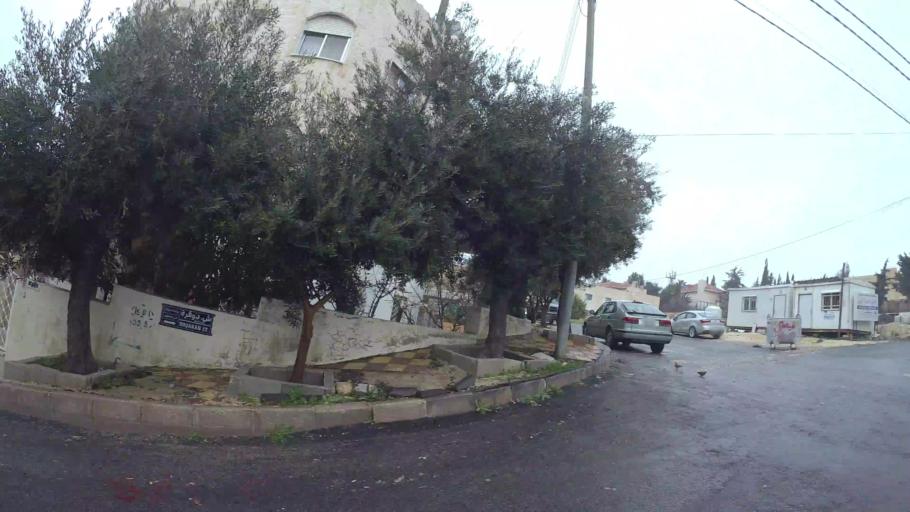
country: JO
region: Amman
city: Al Jubayhah
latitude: 32.0211
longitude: 35.8332
